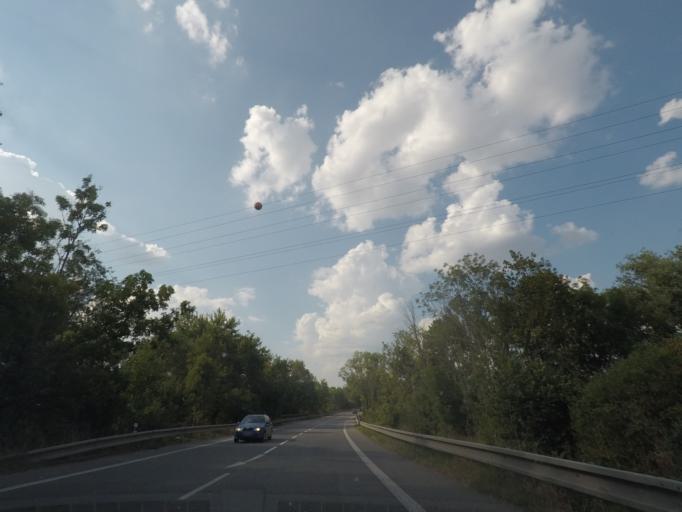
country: CZ
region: Kralovehradecky
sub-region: Okres Nachod
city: Jaromer
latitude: 50.4070
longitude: 15.8864
